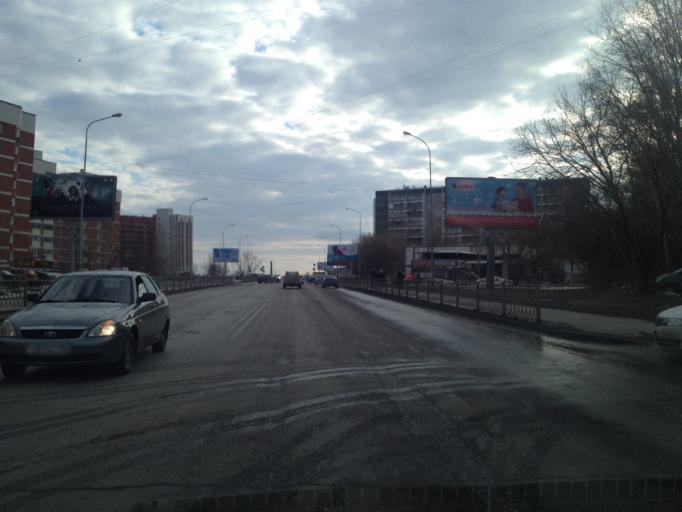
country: RU
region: Sverdlovsk
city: Yekaterinburg
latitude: 56.8514
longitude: 60.5696
